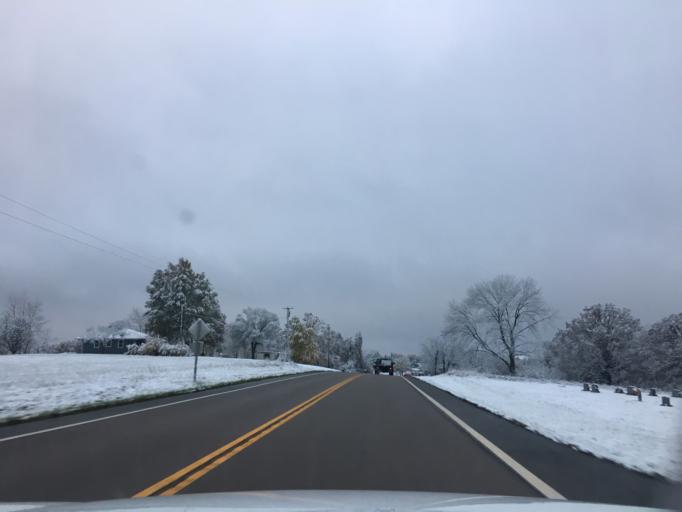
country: US
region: Missouri
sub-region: Osage County
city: Linn
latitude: 38.4708
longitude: -91.8008
